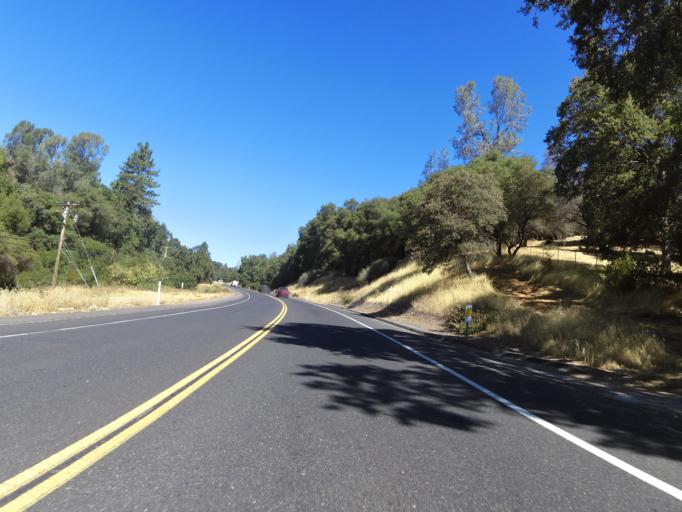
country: US
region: California
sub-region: Calaveras County
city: Murphys
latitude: 38.1252
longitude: -120.4504
